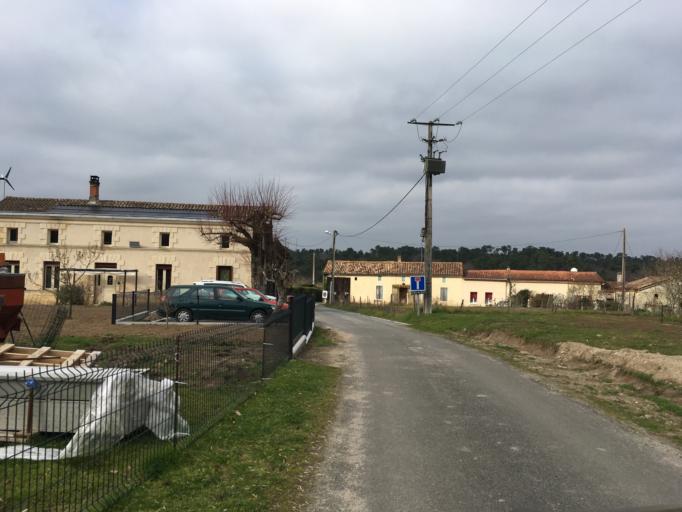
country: FR
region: Aquitaine
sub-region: Departement de la Gironde
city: Saint-Ciers-sur-Gironde
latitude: 45.3213
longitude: -0.6047
